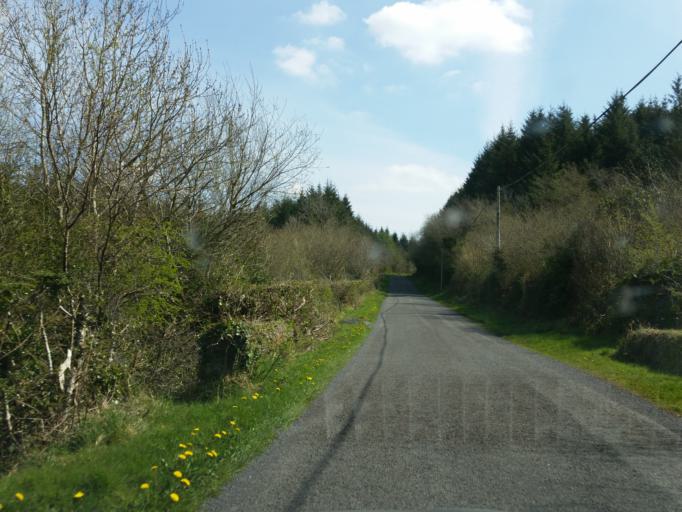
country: GB
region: Northern Ireland
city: Fivemiletown
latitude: 54.3088
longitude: -7.3435
